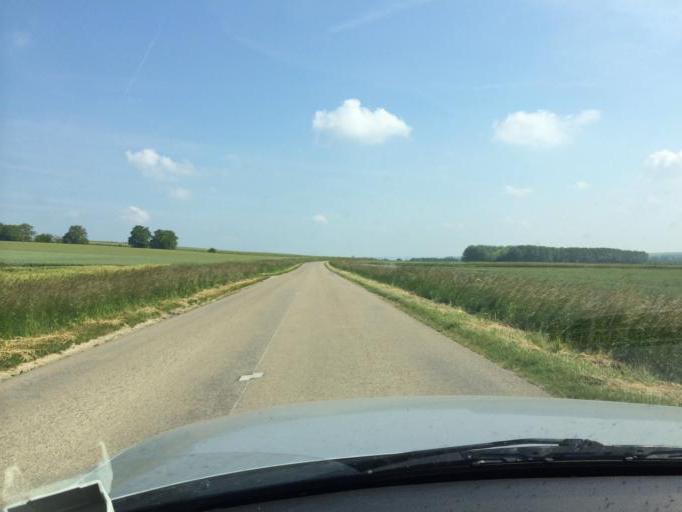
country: FR
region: Bourgogne
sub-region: Departement de l'Yonne
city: Fleury-la-Vallee
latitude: 47.9033
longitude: 3.4316
